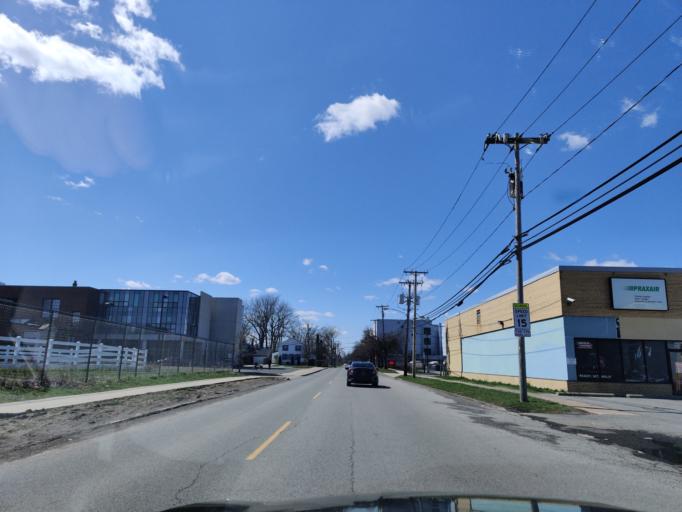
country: US
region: New York
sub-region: Erie County
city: Kenmore
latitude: 42.9420
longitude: -78.8706
